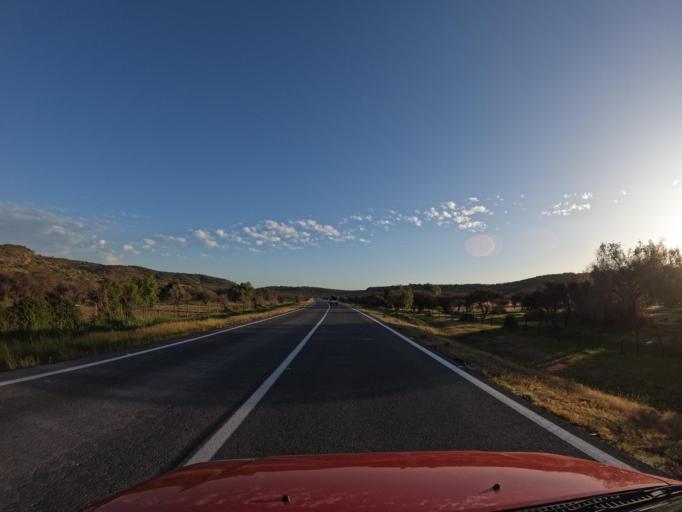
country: CL
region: O'Higgins
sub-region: Provincia de Colchagua
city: Santa Cruz
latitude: -34.3060
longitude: -71.7366
